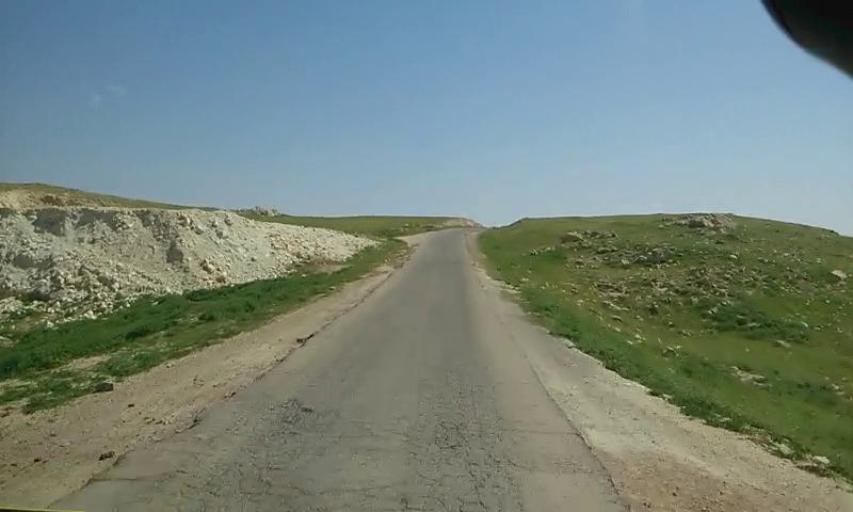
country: PS
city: `Arab ar Rashaydah
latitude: 31.5467
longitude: 35.2575
